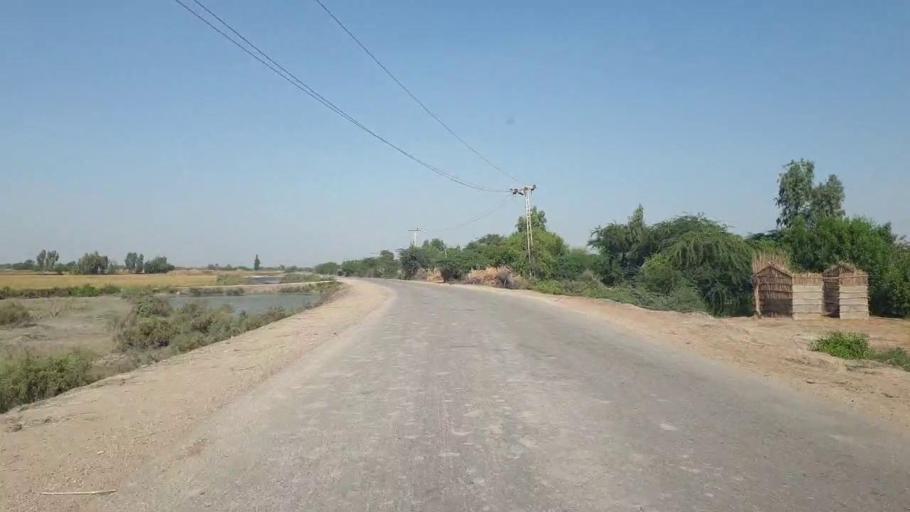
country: PK
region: Sindh
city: Talhar
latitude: 24.9206
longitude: 68.8615
